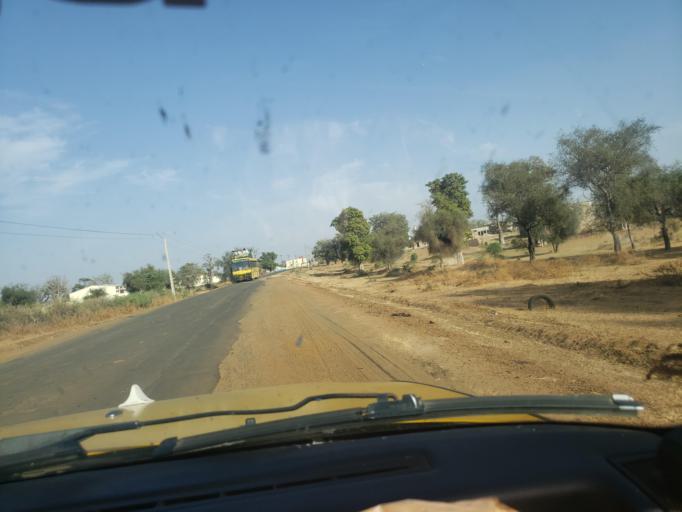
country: SN
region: Louga
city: Louga
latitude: 15.5127
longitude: -15.9985
